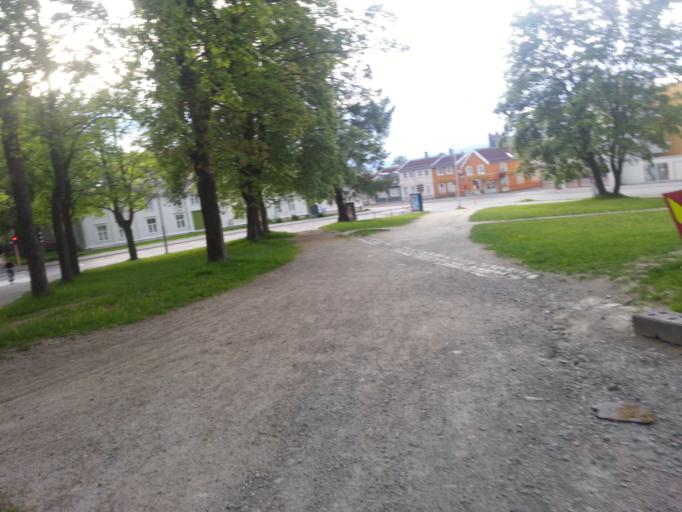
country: NO
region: Sor-Trondelag
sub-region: Trondheim
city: Trondheim
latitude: 63.4214
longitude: 10.3999
